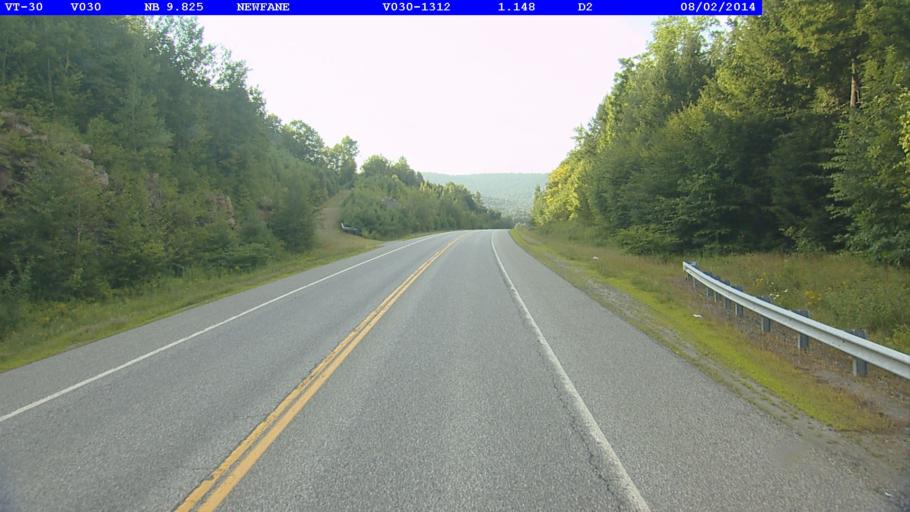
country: US
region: Vermont
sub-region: Windham County
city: Newfane
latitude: 42.9615
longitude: -72.6527
